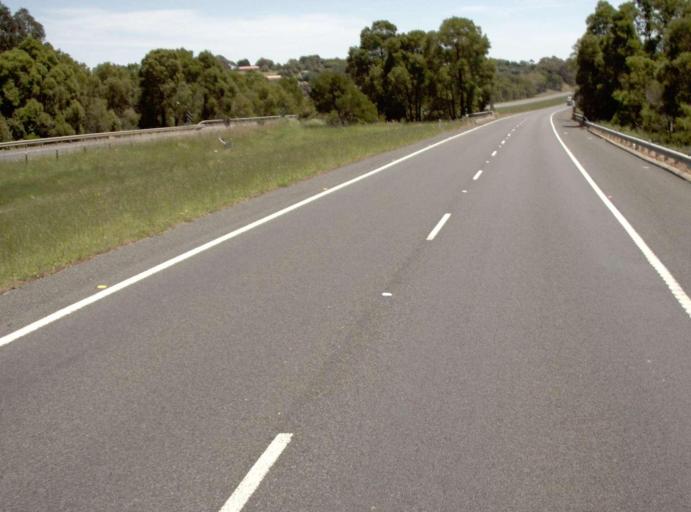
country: AU
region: Victoria
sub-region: Baw Baw
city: Warragul
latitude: -38.1312
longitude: 145.8778
